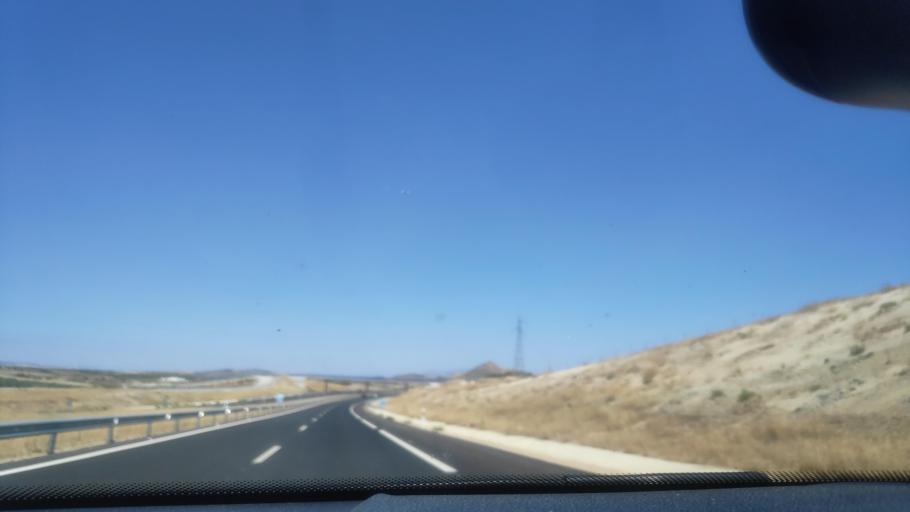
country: ES
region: Andalusia
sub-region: Provincia de Granada
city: Otura
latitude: 37.0716
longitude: -3.6574
